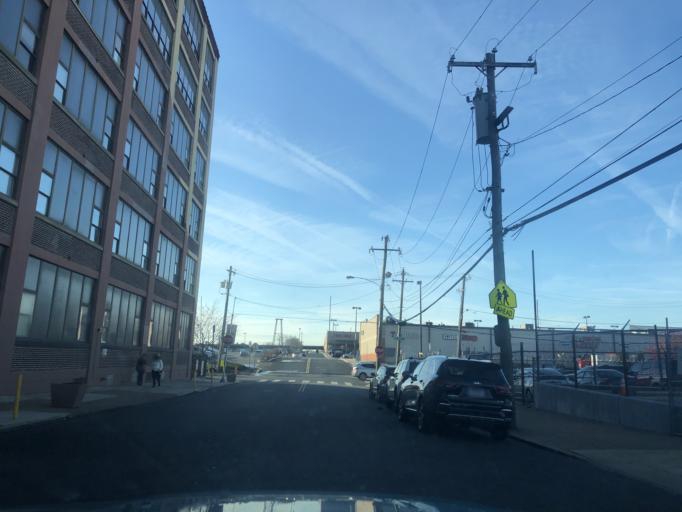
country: US
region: Pennsylvania
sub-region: Montgomery County
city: Bala-Cynwyd
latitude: 39.9800
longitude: -75.2220
